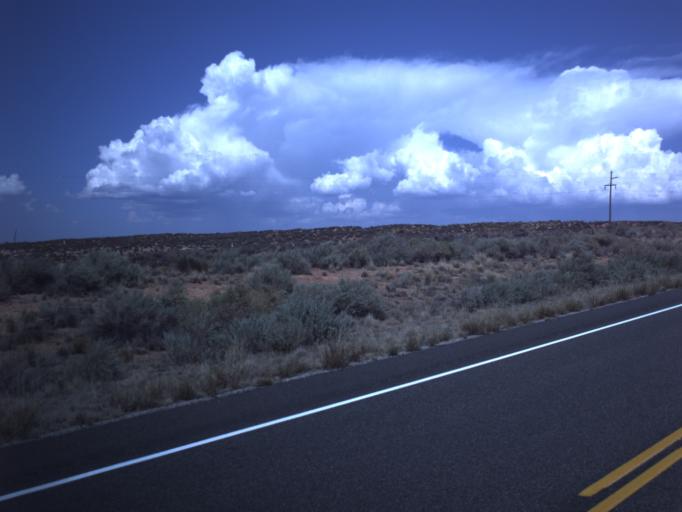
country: US
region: Utah
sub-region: San Juan County
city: Blanding
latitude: 37.3473
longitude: -109.5191
